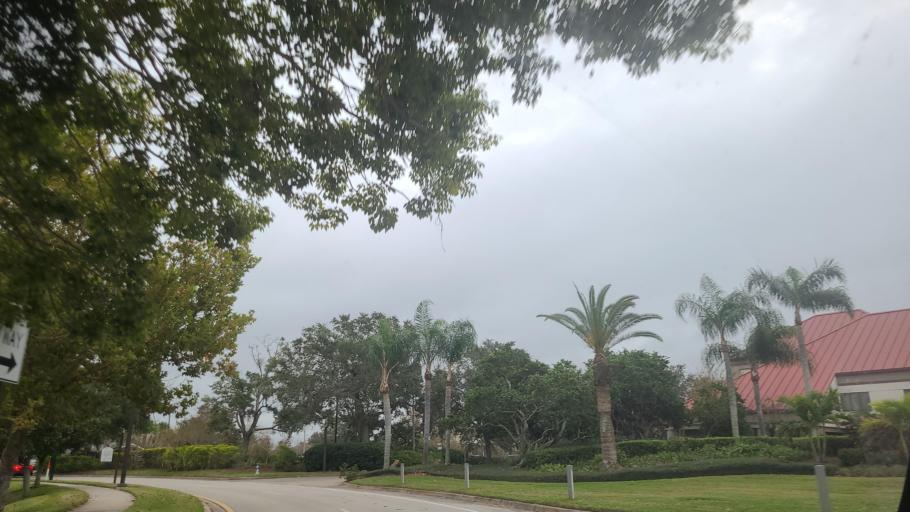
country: US
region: Florida
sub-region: Orange County
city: Conway
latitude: 28.4566
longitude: -81.3076
